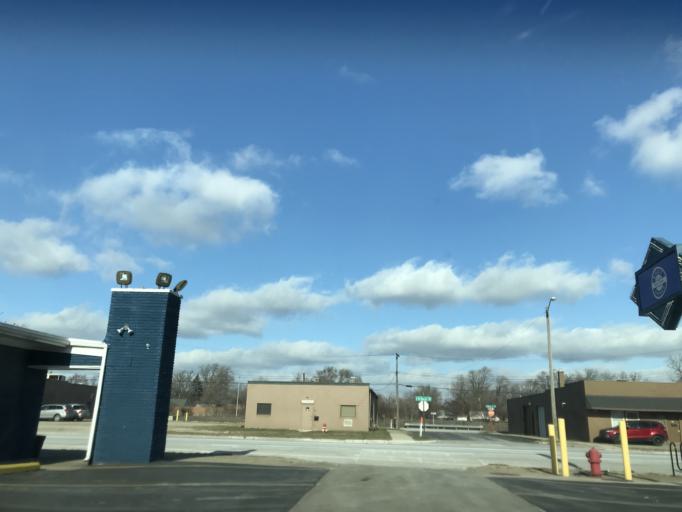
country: US
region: Michigan
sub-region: Oakland County
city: Madison Heights
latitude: 42.4759
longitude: -83.1018
